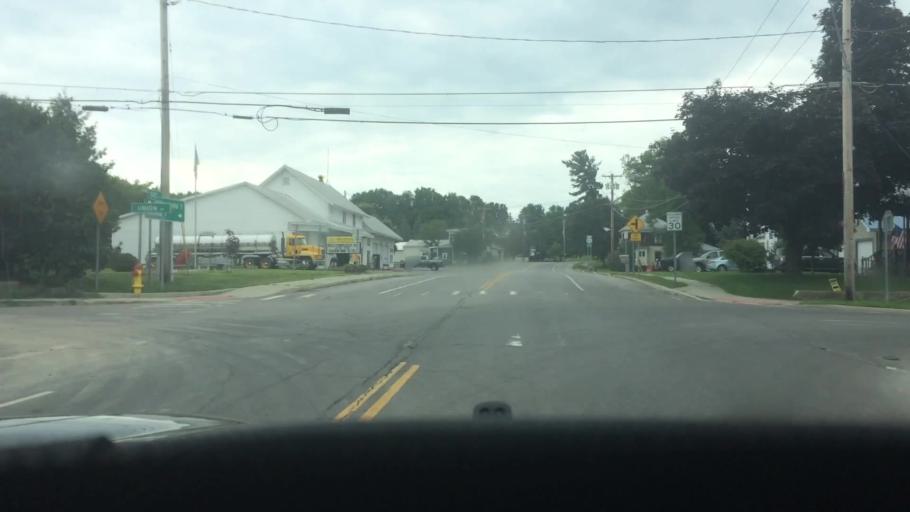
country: US
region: New York
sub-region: St. Lawrence County
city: Ogdensburg
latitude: 44.6165
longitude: -75.4048
